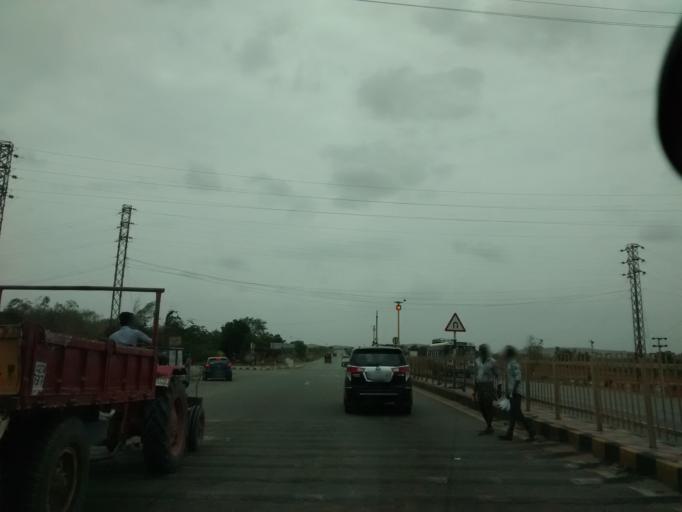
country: IN
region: Andhra Pradesh
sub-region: Anantapur
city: Anantapur
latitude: 14.8114
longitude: 77.5988
